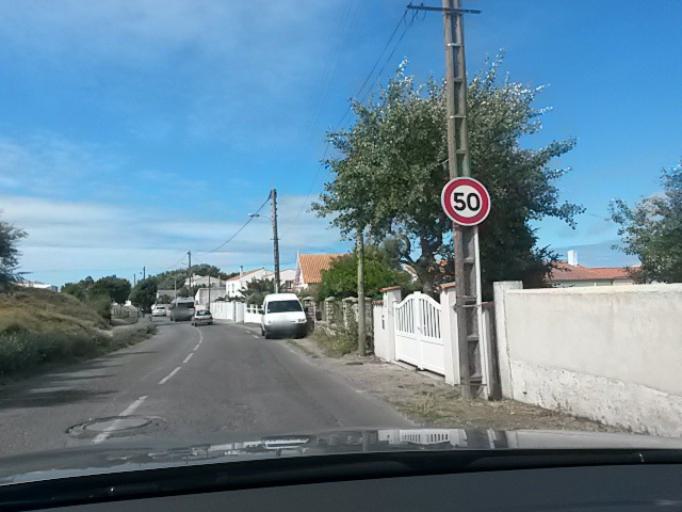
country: FR
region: Poitou-Charentes
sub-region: Departement de la Charente-Maritime
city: Dolus-d'Oleron
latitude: 45.9140
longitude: -1.3229
